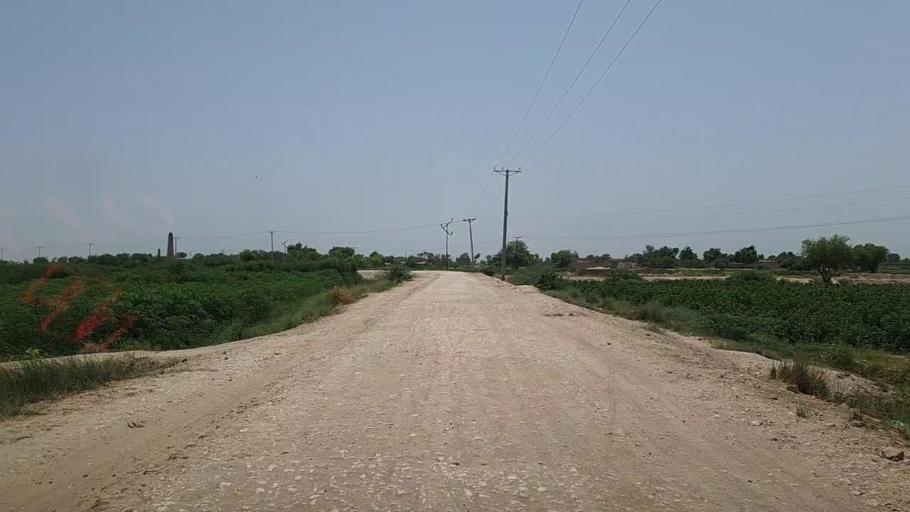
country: PK
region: Sindh
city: Pad Idan
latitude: 26.7721
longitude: 68.2919
